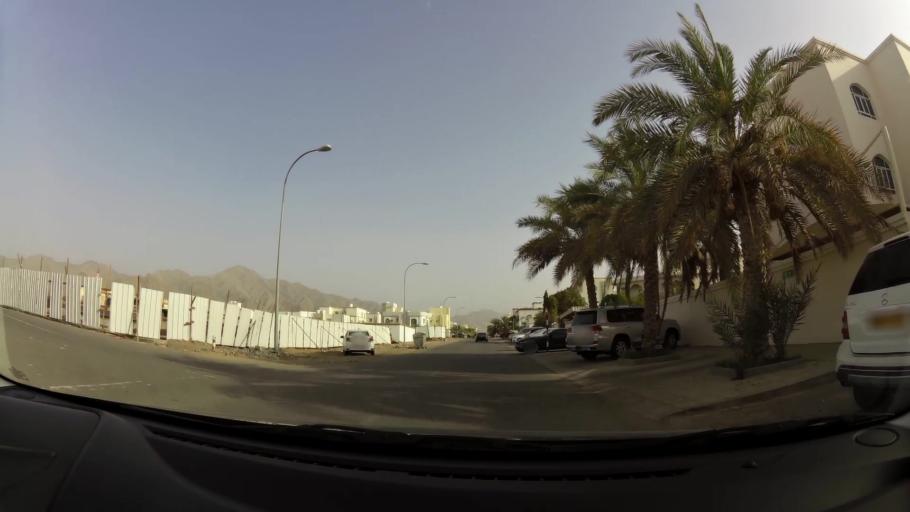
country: OM
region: Muhafazat Masqat
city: Bawshar
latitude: 23.5422
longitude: 58.3598
